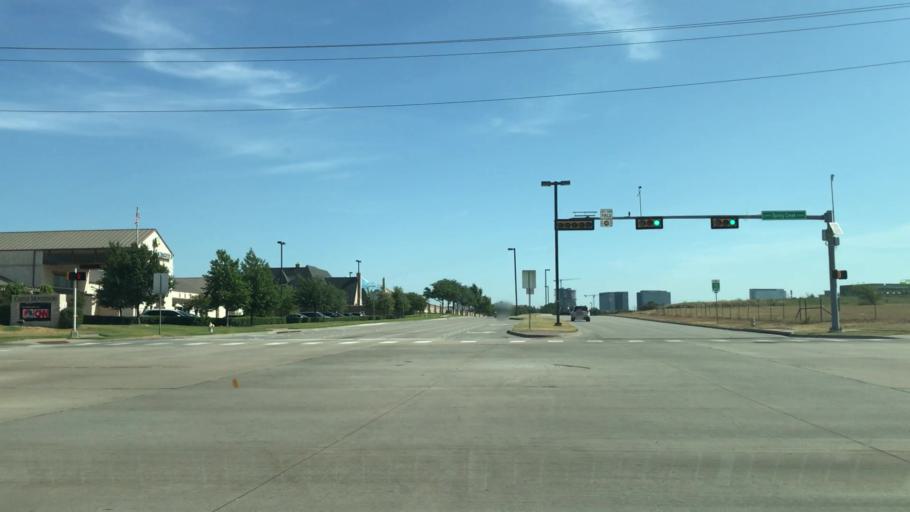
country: US
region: Texas
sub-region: Denton County
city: The Colony
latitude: 33.0667
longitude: -96.8390
